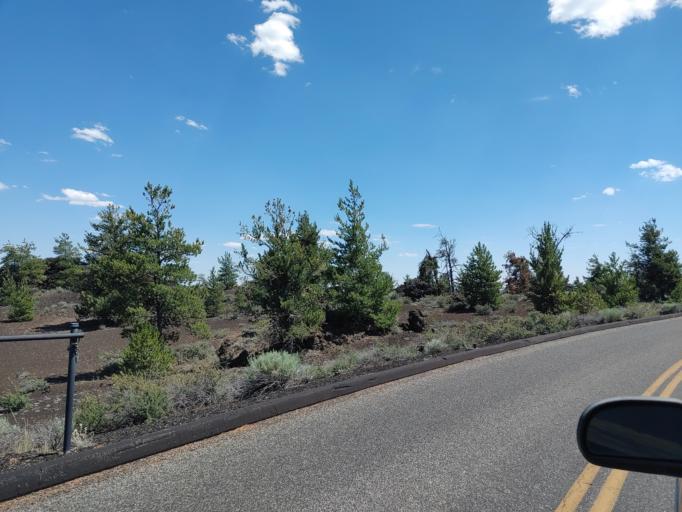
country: US
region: Idaho
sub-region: Butte County
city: Arco
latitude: 43.4515
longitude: -113.5430
